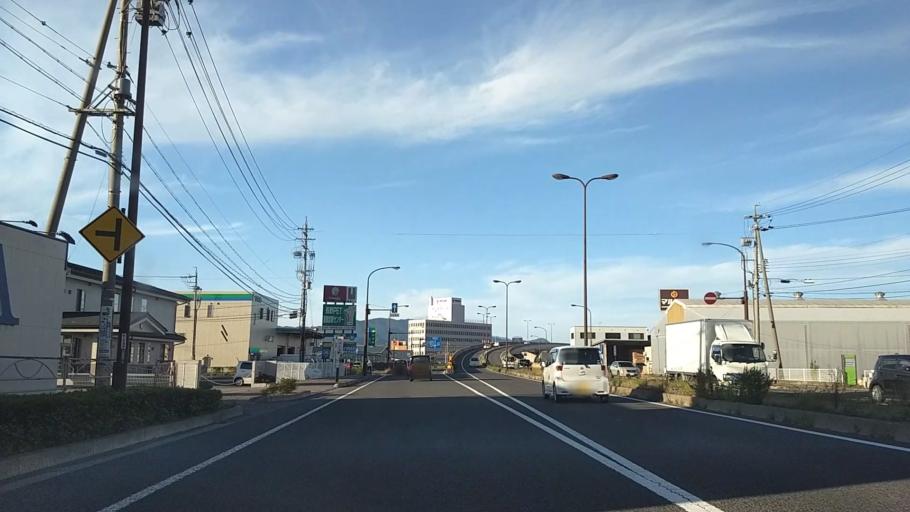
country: JP
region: Nagano
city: Nagano-shi
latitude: 36.6262
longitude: 138.2006
